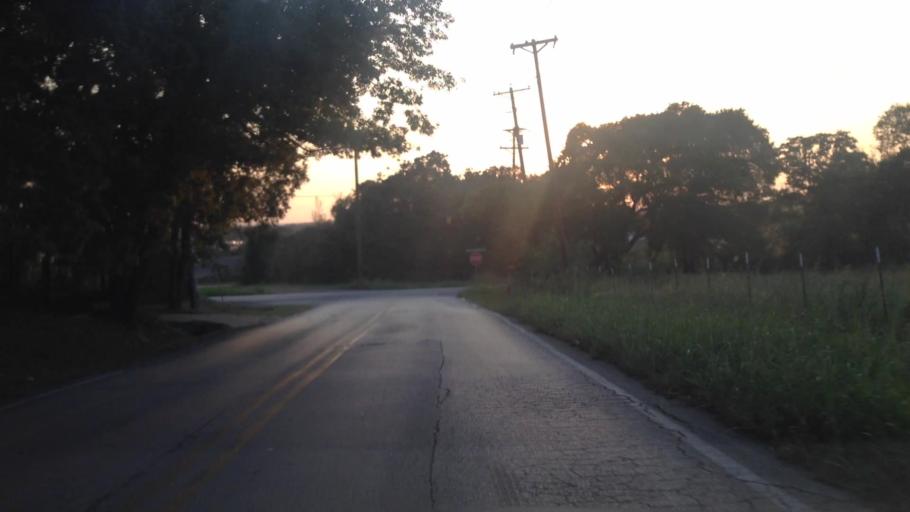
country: US
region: Texas
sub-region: Tarrant County
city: Kennedale
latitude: 32.6333
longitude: -97.2015
